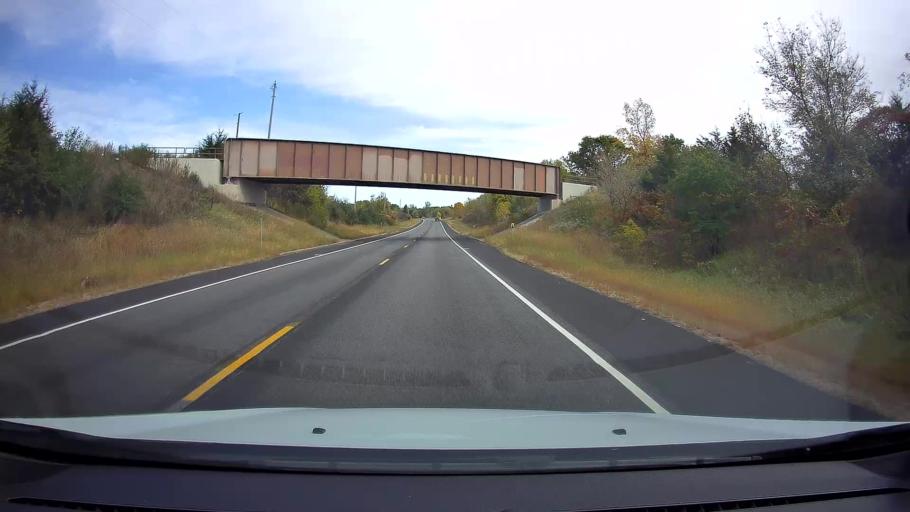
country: US
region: Minnesota
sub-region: Washington County
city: Stillwater
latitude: 45.1228
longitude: -92.7671
